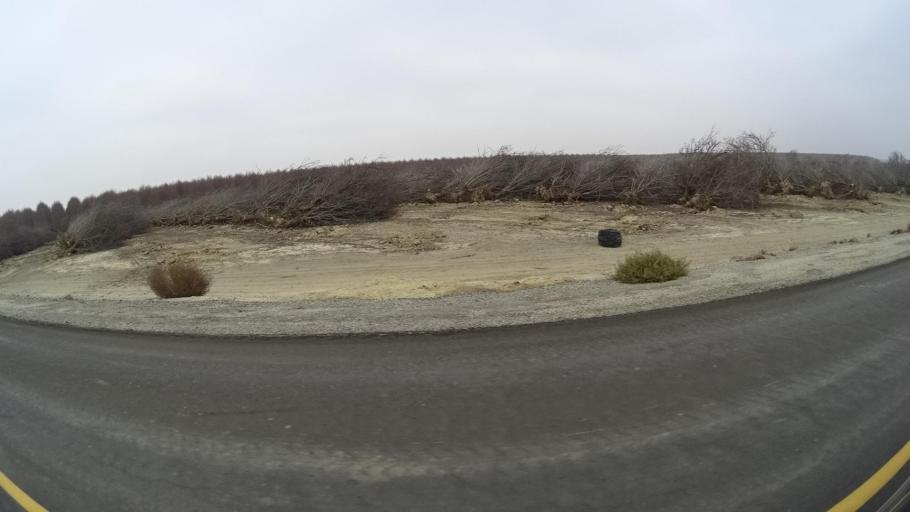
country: US
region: California
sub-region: Kern County
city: Maricopa
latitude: 35.1184
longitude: -119.3568
